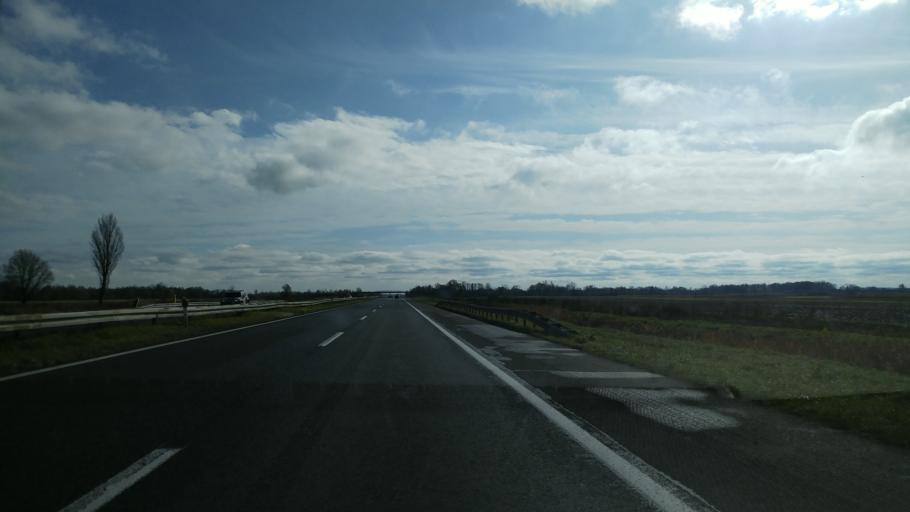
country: HR
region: Zagrebacka
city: Lupoglav
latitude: 45.7234
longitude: 16.3433
